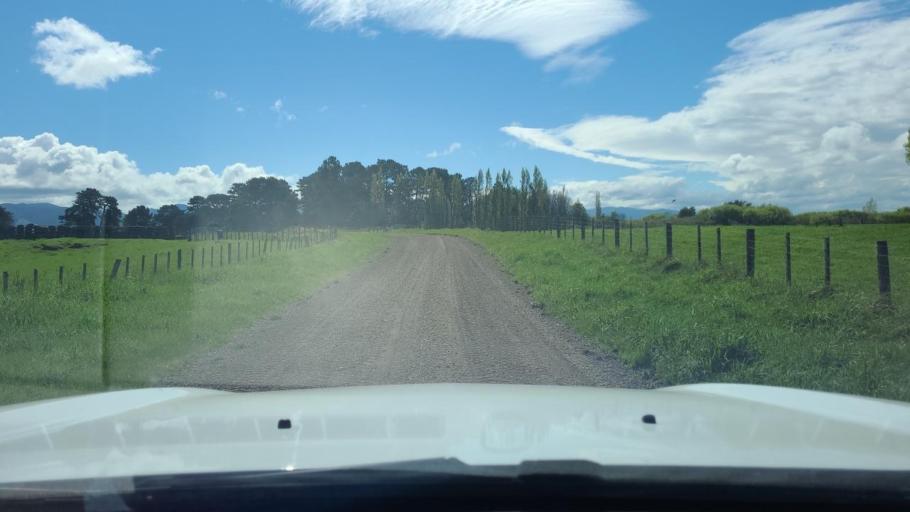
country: NZ
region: Wellington
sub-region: Upper Hutt City
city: Upper Hutt
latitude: -41.2616
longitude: 175.2784
